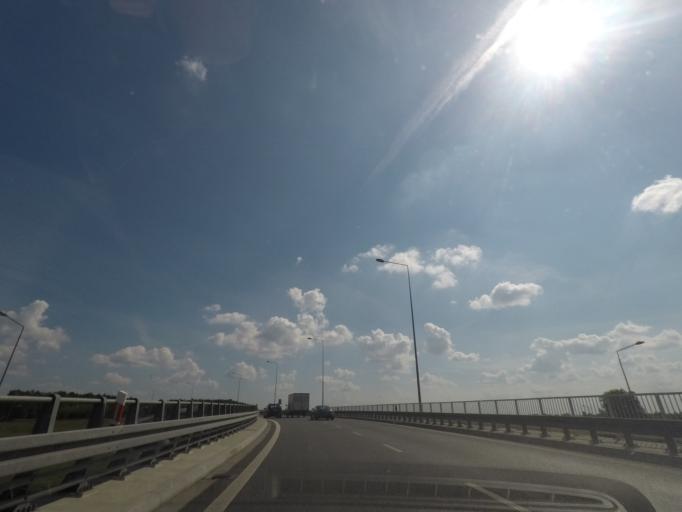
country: PL
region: Lodz Voivodeship
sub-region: Powiat zgierski
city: Strykow
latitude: 51.8913
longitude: 19.6319
